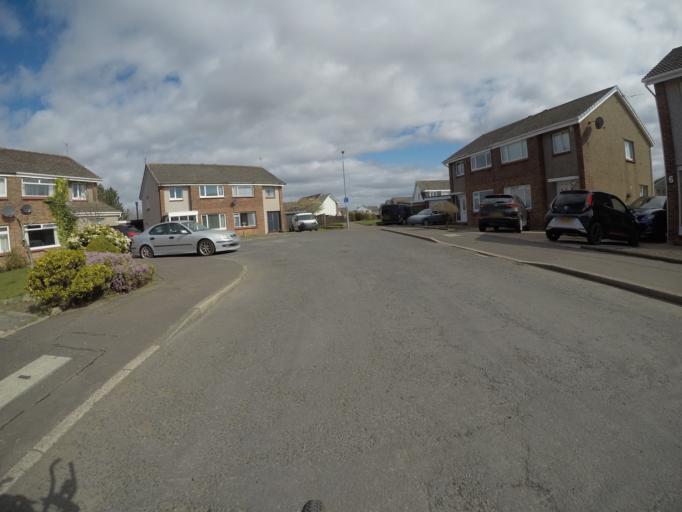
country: GB
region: Scotland
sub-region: South Ayrshire
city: Troon
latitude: 55.5652
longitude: -4.6437
